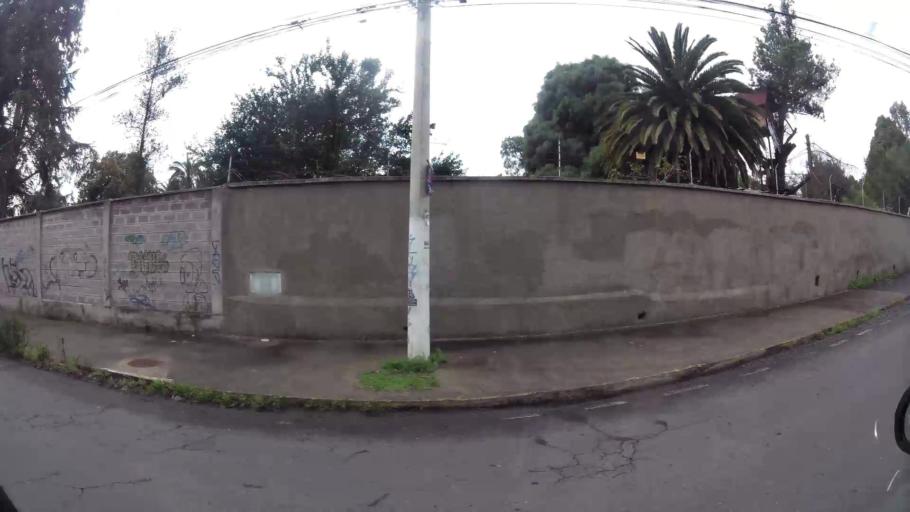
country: EC
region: Pichincha
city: Sangolqui
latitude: -0.2995
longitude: -78.4814
